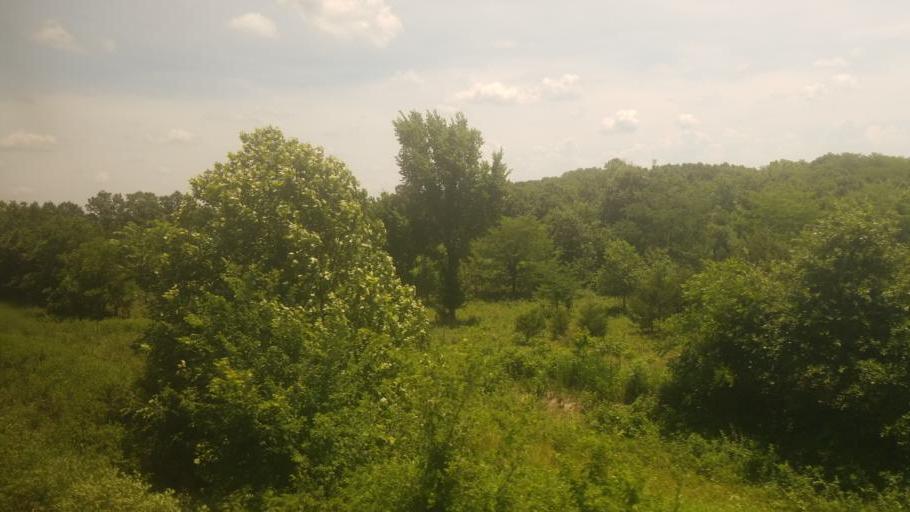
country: US
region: Missouri
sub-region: Linn County
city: Marceline
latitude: 39.8655
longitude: -92.7975
